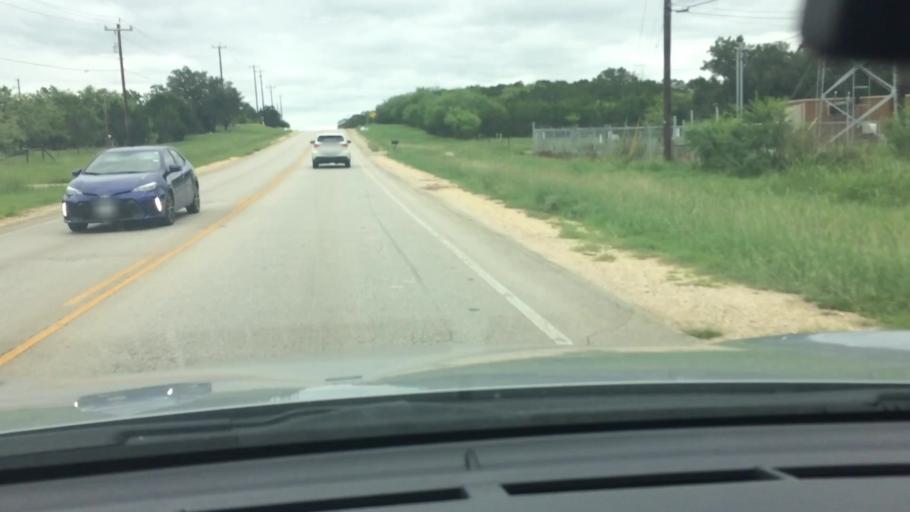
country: US
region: Texas
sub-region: Comal County
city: Garden Ridge
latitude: 29.6434
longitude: -98.3929
